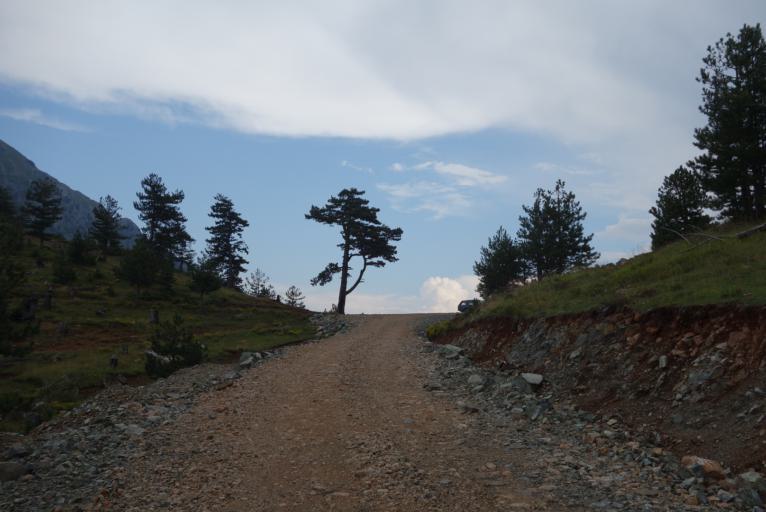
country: AL
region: Diber
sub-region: Rrethi i Dibres
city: Fushe-Lure
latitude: 41.7735
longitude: 20.2221
